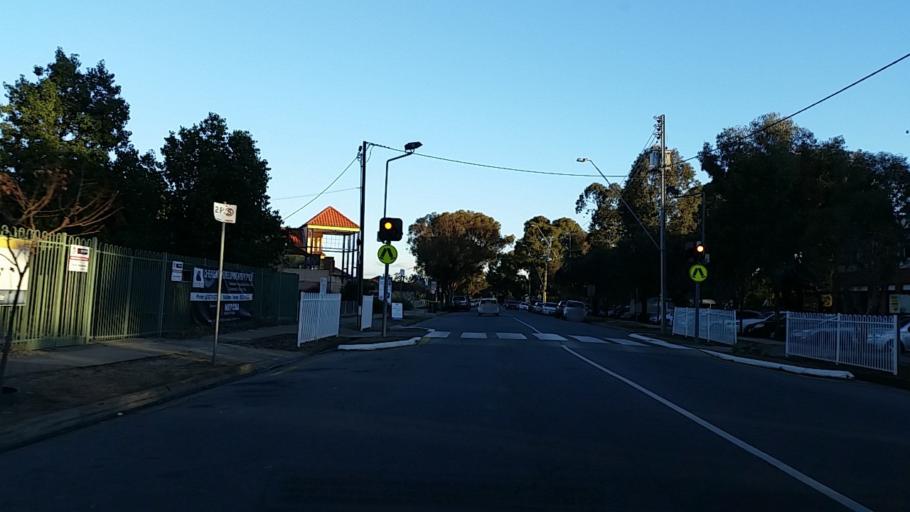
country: AU
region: South Australia
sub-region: Salisbury
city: Salisbury
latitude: -34.7632
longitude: 138.6483
